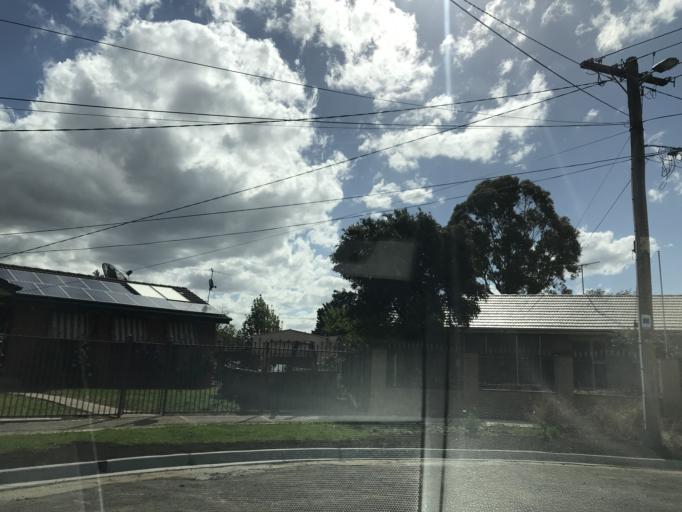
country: AU
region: Victoria
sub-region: Brimbank
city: Sunshine West
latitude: -37.8024
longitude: 144.8172
